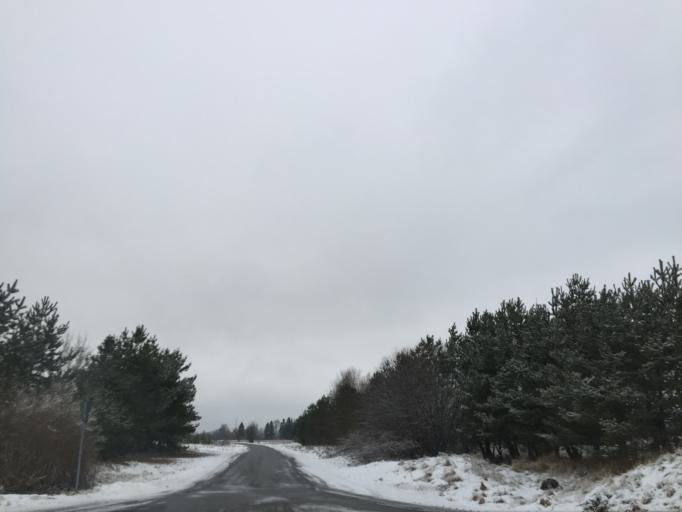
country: EE
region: Laeaene
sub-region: Lihula vald
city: Lihula
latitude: 58.6743
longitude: 23.8299
